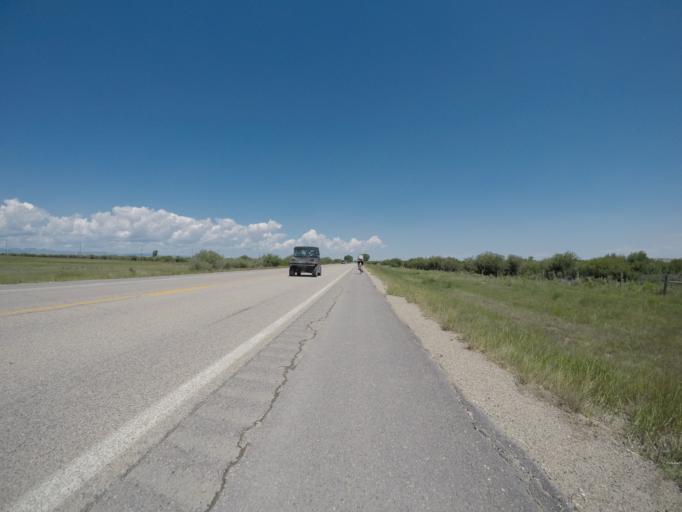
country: US
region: Wyoming
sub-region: Sublette County
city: Marbleton
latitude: 42.5202
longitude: -110.1062
